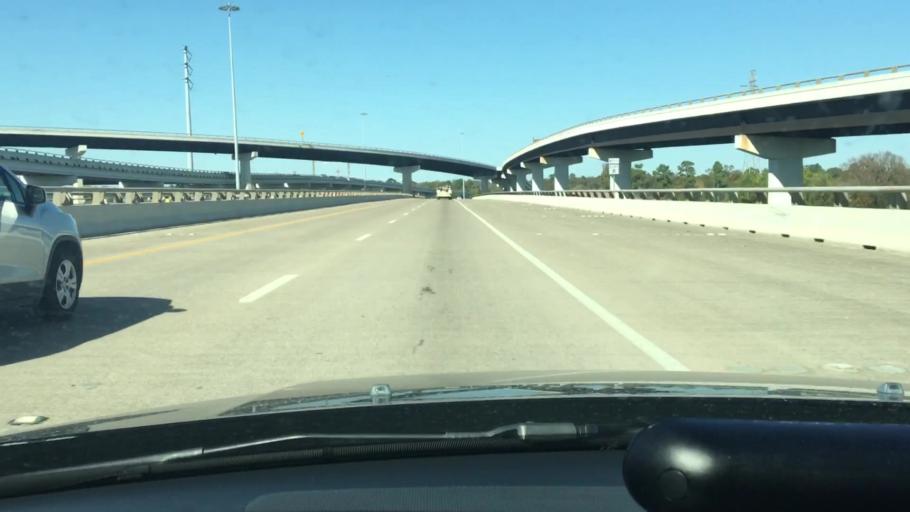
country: US
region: Texas
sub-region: Harris County
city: Cloverleaf
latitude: 29.7722
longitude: -95.1541
